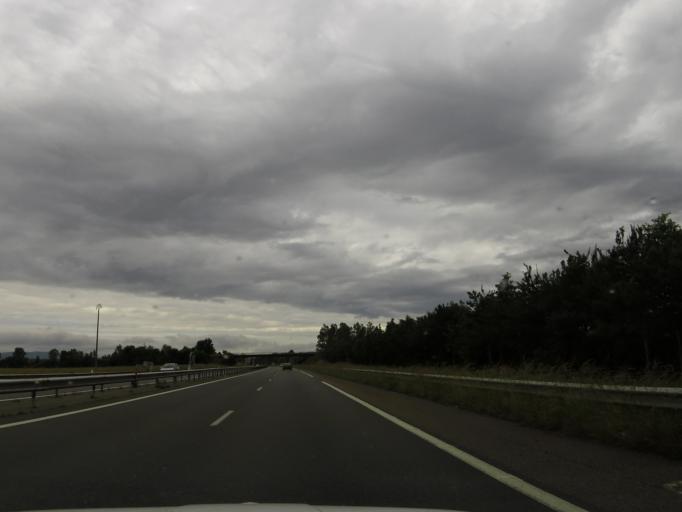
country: FR
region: Rhone-Alpes
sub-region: Departement de la Loire
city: Saint-Germain-Laval
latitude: 45.8469
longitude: 4.0813
